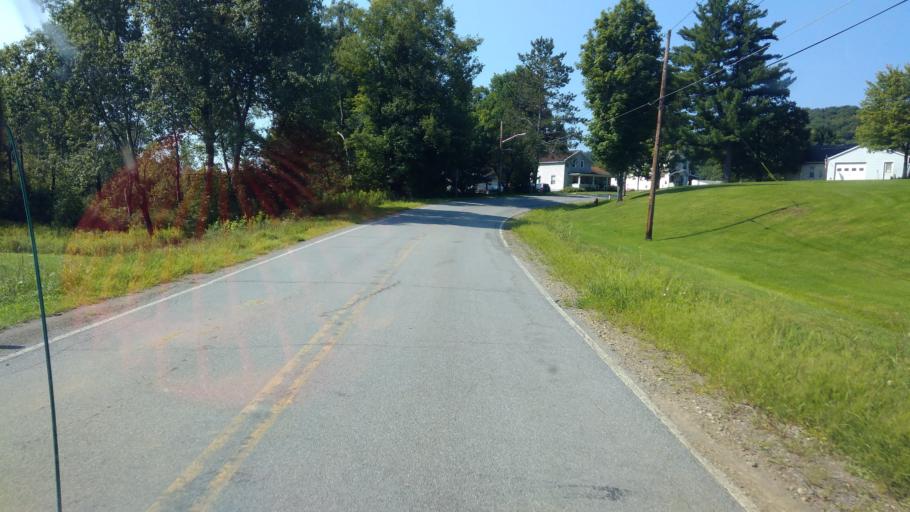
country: US
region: New York
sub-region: Allegany County
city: Bolivar
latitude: 42.0890
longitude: -78.1573
